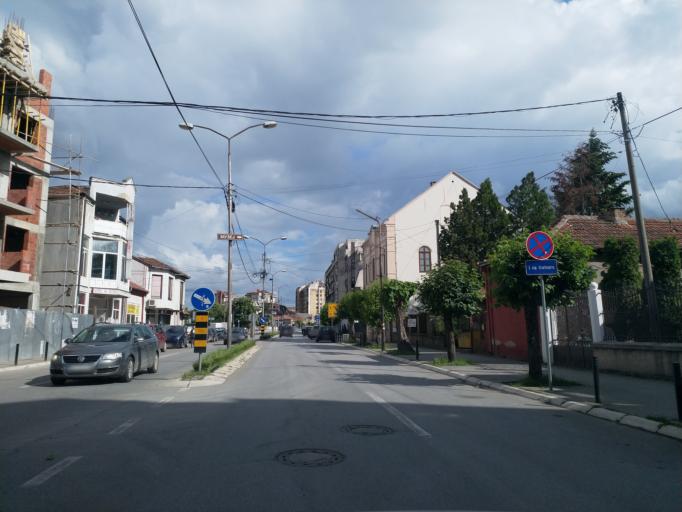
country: RS
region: Central Serbia
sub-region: Pomoravski Okrug
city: Paracin
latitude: 43.8646
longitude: 21.4085
